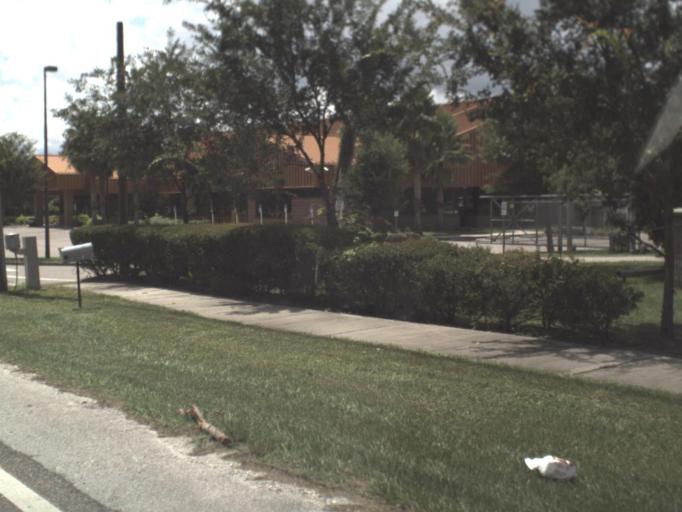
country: US
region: Florida
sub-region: Hillsborough County
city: Dover
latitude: 27.9953
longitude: -82.2169
